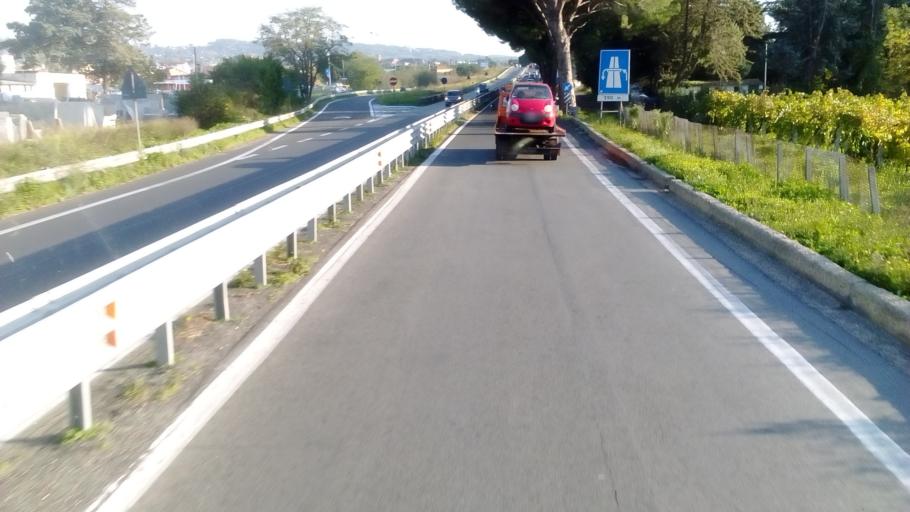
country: IT
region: Latium
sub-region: Citta metropolitana di Roma Capitale
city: Ciampino
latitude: 41.7807
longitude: 12.6034
